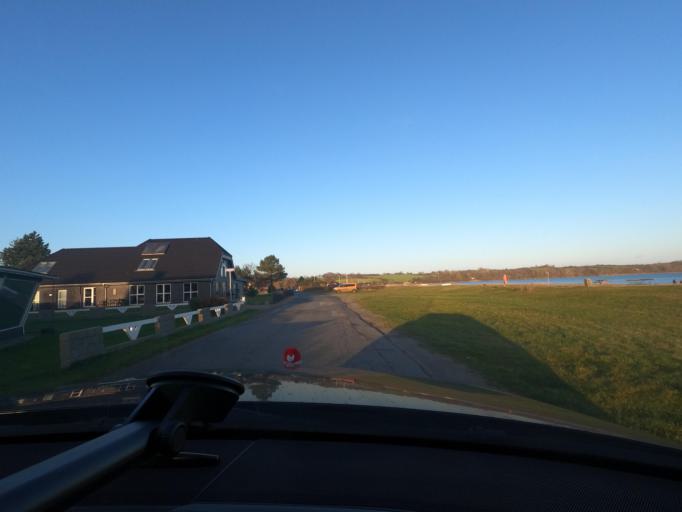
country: DK
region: South Denmark
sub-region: Sonderborg Kommune
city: Broager
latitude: 54.8973
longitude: 9.7013
